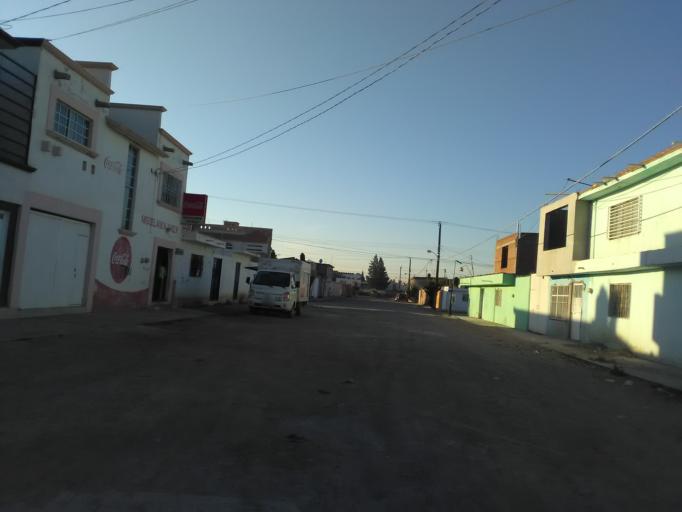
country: MX
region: Durango
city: Victoria de Durango
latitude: 24.0517
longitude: -104.6384
